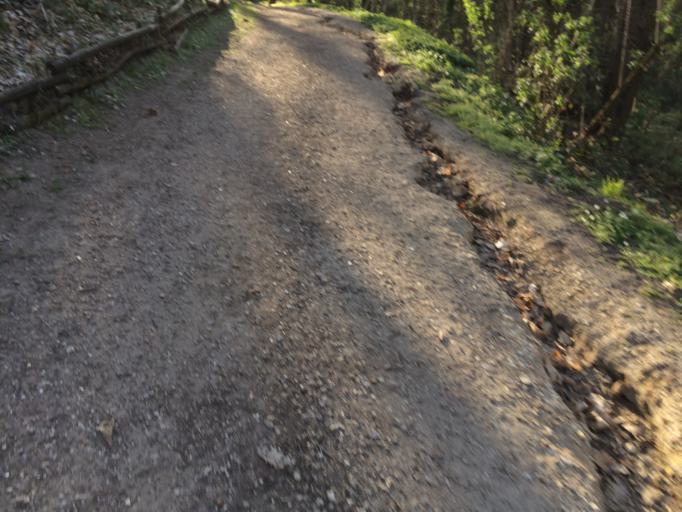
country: FR
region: Ile-de-France
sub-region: Departement de l'Essonne
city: Villejust
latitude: 48.6930
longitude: 2.2243
